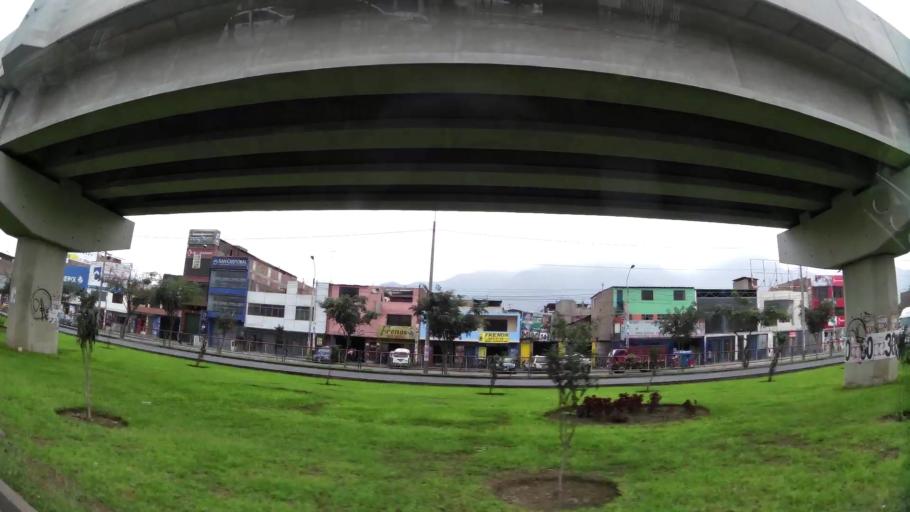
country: PE
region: Lima
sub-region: Lima
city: Independencia
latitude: -11.9982
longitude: -77.0096
